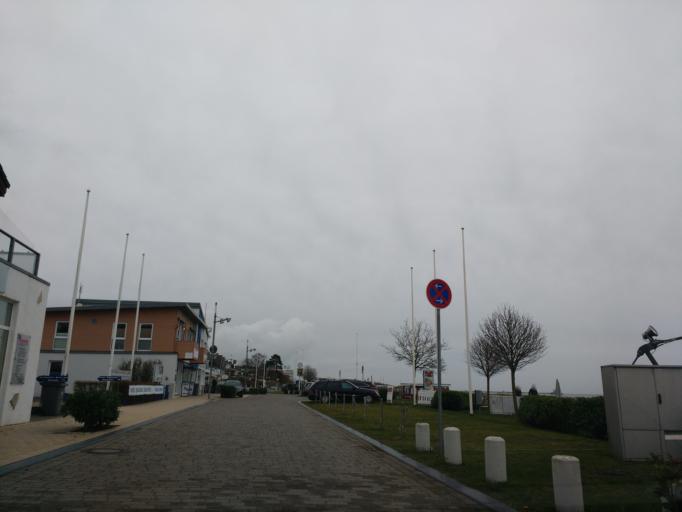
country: DE
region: Schleswig-Holstein
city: Gromitz
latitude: 54.1368
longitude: 10.9467
